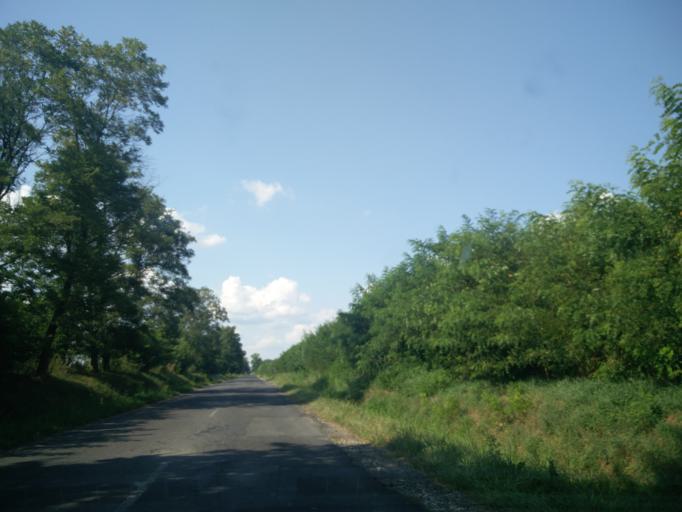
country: HU
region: Zala
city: Zalaegerszeg
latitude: 46.8764
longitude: 16.7940
